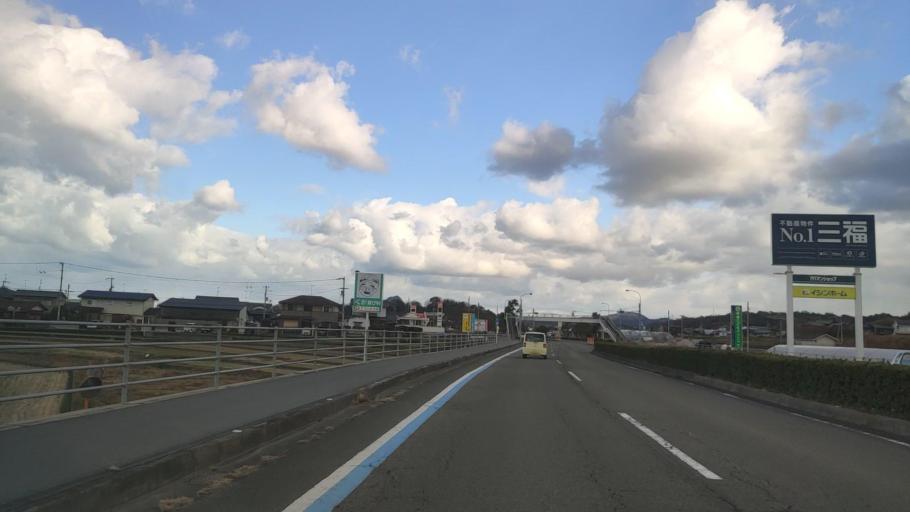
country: JP
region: Ehime
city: Hojo
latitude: 33.9418
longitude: 132.7745
